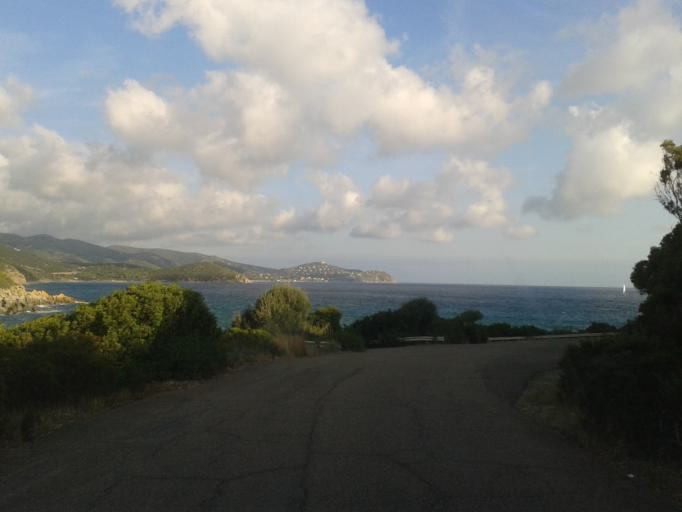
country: IT
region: Sardinia
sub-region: Provincia di Cagliari
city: Quartu Sant'Elena
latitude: 39.1794
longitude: 9.3539
